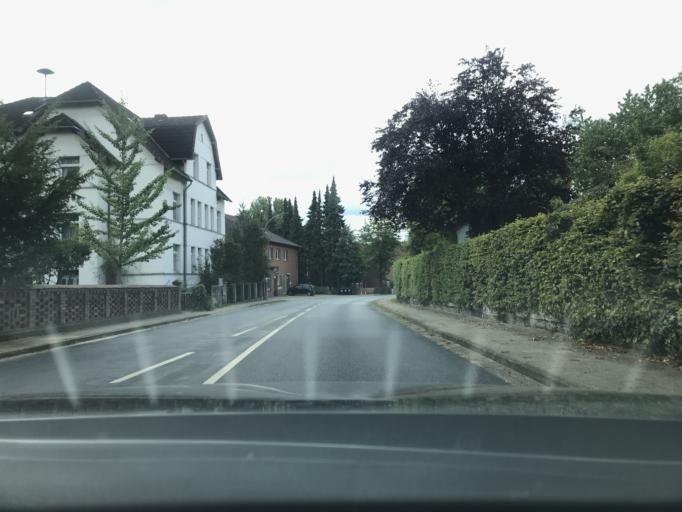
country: DE
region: Lower Saxony
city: Suderburg
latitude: 52.8938
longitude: 10.4454
